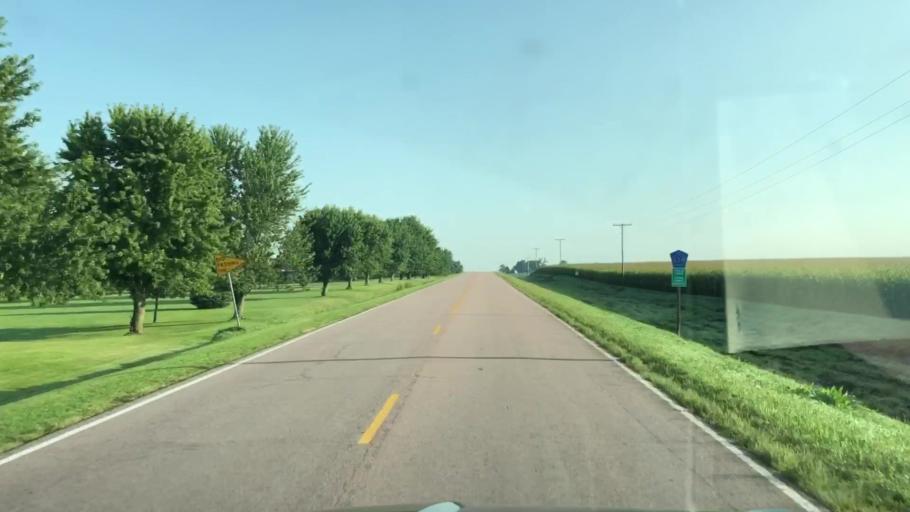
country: US
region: Iowa
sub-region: Lyon County
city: George
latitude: 43.2585
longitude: -96.0001
